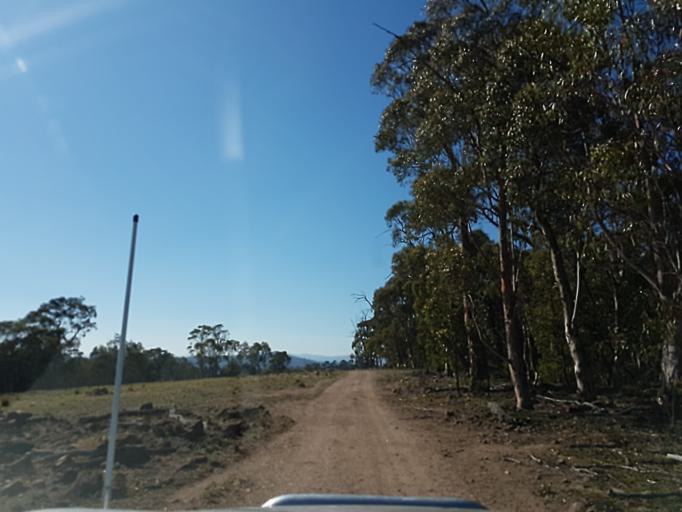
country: AU
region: New South Wales
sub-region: Snowy River
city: Jindabyne
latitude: -37.0391
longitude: 148.2816
